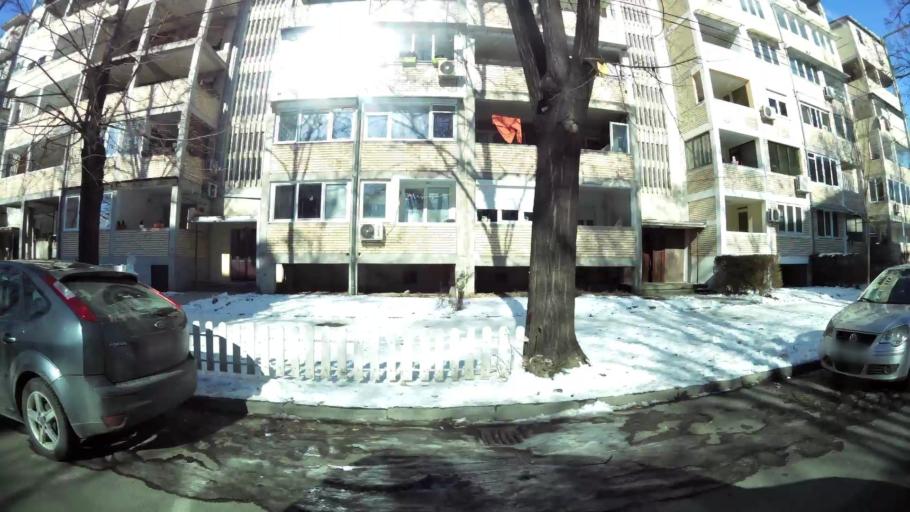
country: MK
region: Saraj
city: Saraj
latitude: 42.0048
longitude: 21.3534
